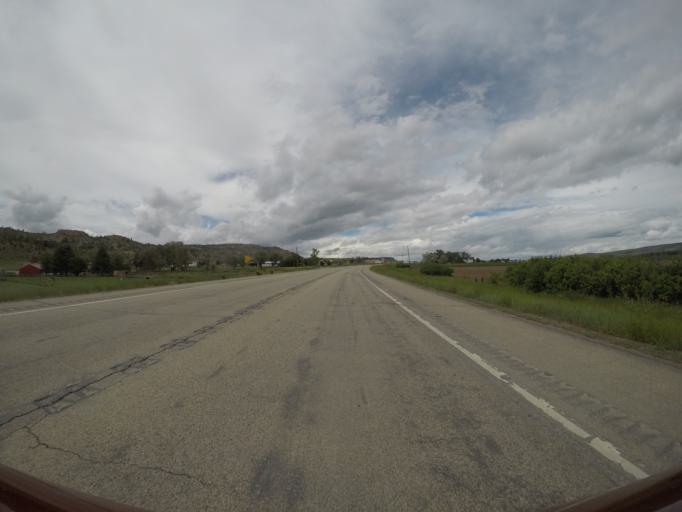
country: US
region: Montana
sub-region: Carbon County
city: Red Lodge
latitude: 45.2719
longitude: -108.9174
